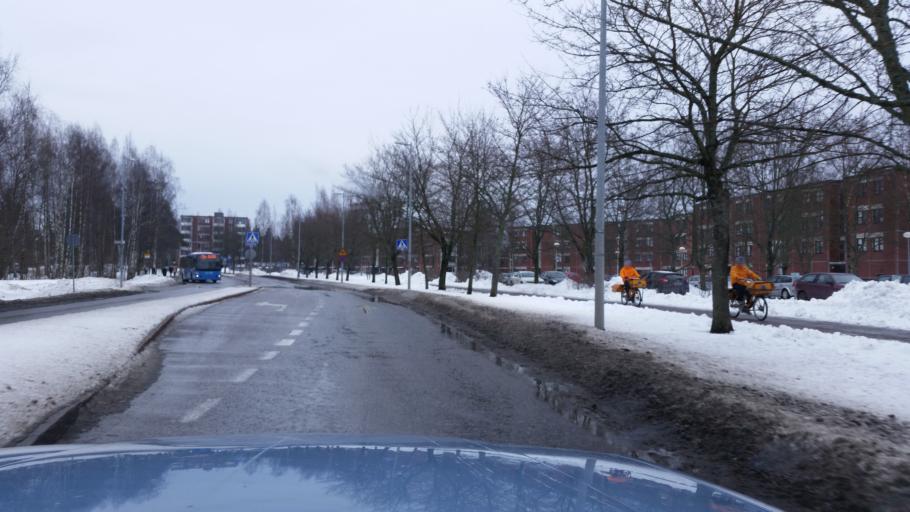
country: FI
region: Uusimaa
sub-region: Helsinki
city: Vantaa
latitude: 60.2781
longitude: 25.0225
